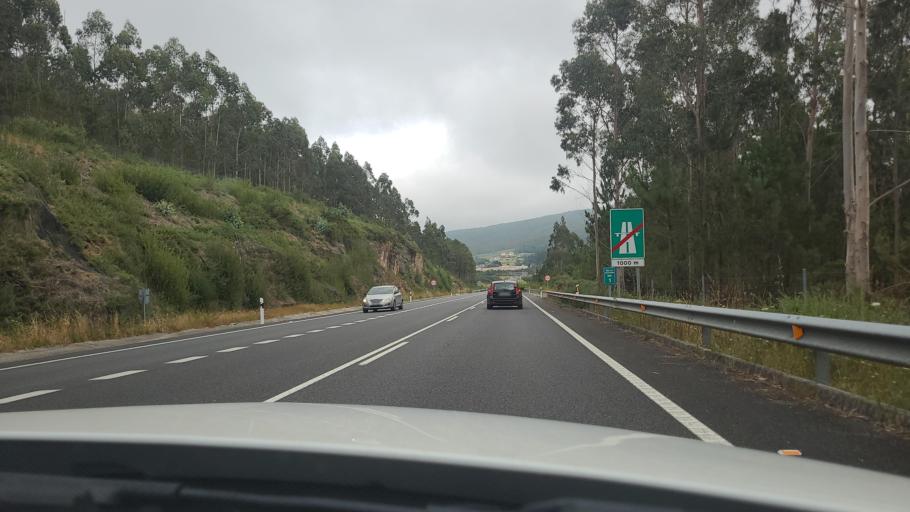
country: ES
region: Galicia
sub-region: Provincia da Coruna
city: Cee
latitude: 42.9714
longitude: -9.1987
